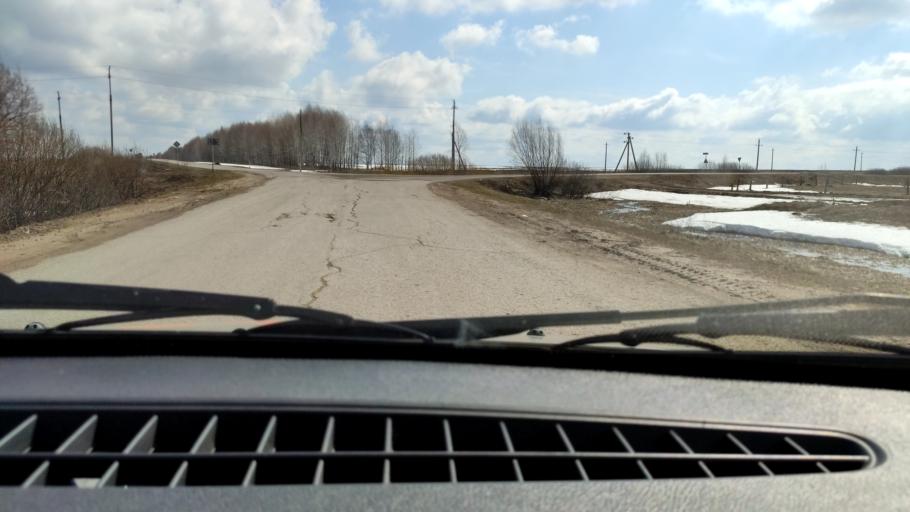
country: RU
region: Bashkortostan
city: Kudeyevskiy
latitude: 54.8513
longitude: 56.7945
